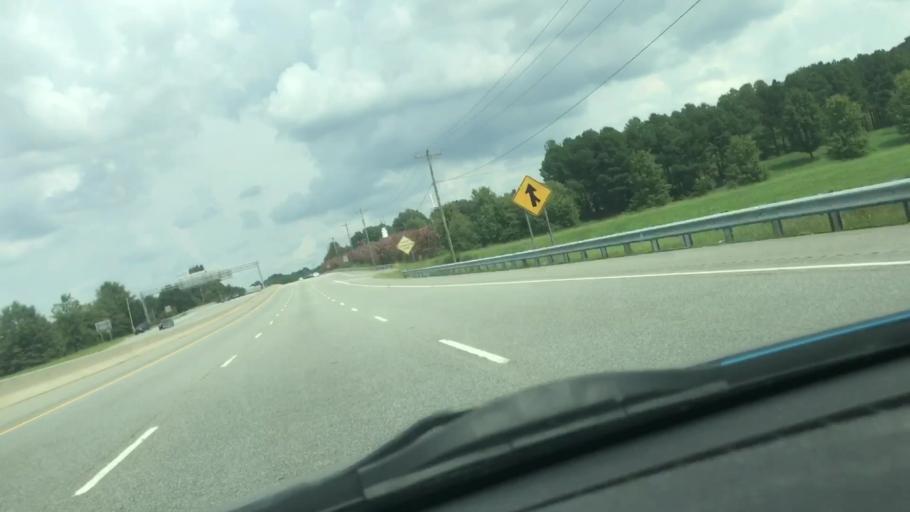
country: US
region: North Carolina
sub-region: Guilford County
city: Greensboro
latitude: 36.0332
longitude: -79.8208
